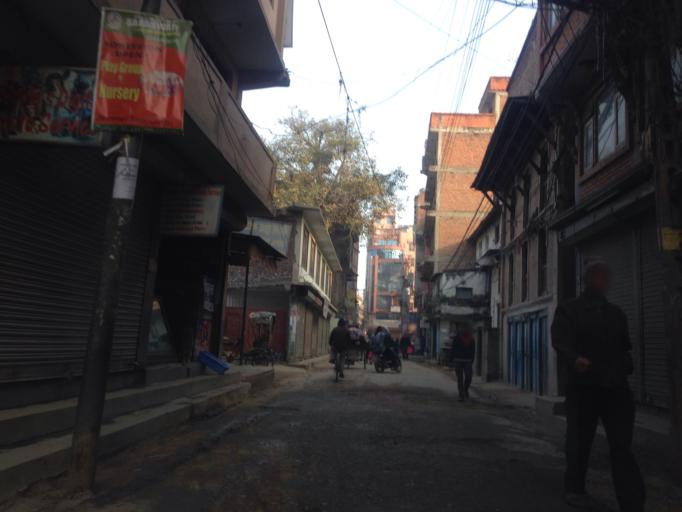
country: NP
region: Central Region
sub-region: Bagmati Zone
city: Kathmandu
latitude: 27.7146
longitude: 85.3085
